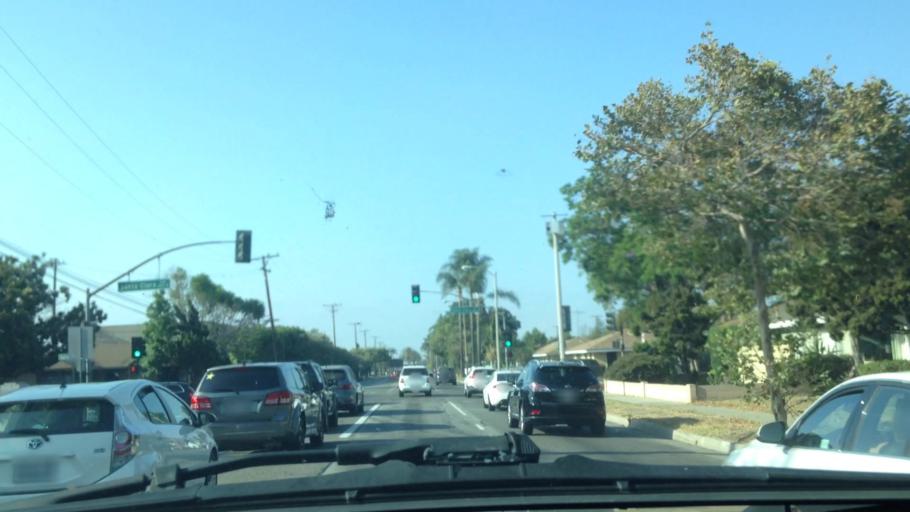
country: US
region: California
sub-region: Orange County
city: Santa Ana
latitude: 33.7674
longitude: -117.8849
